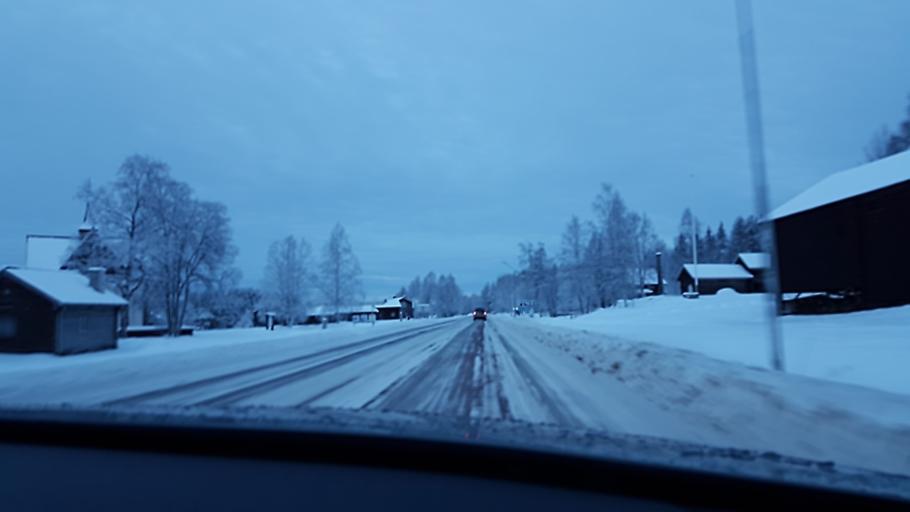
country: SE
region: Jaemtland
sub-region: Harjedalens Kommun
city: Sveg
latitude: 62.0482
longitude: 14.6491
